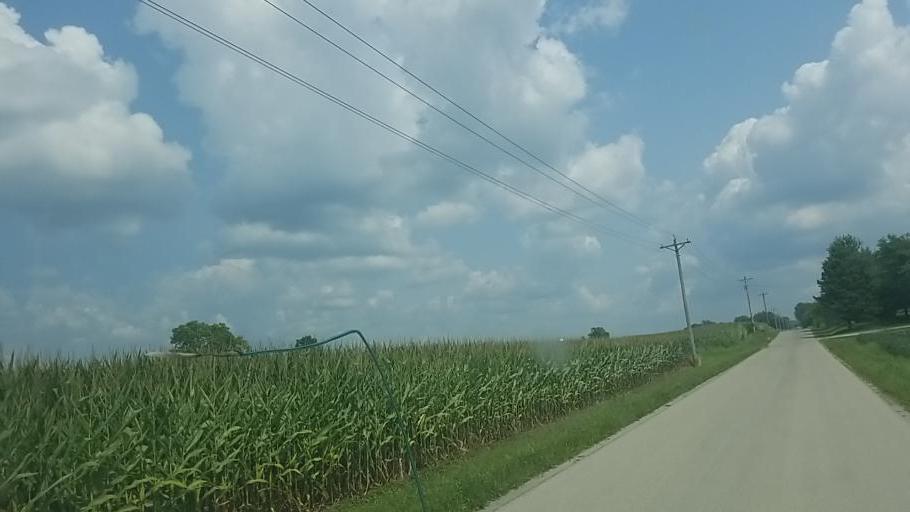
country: US
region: Ohio
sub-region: Wyandot County
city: Upper Sandusky
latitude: 40.9209
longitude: -83.1562
